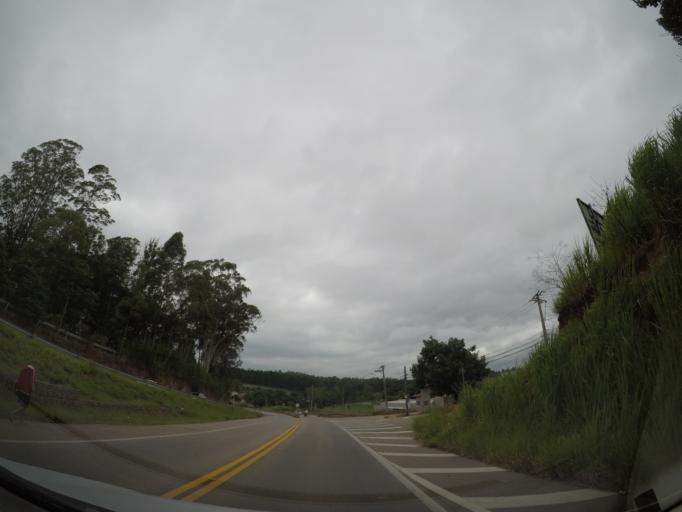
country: BR
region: Sao Paulo
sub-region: Louveira
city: Louveira
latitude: -23.1243
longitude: -46.9337
